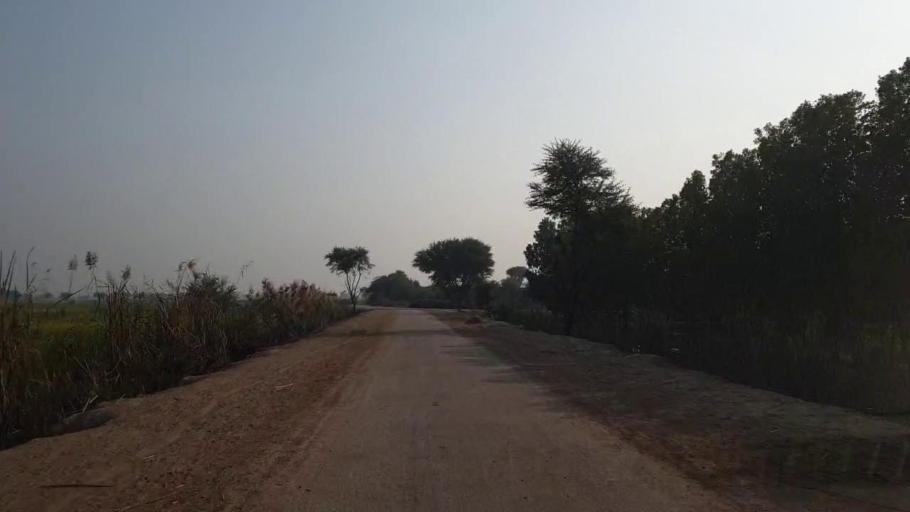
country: PK
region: Sindh
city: Shahdadpur
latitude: 25.9640
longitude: 68.5235
